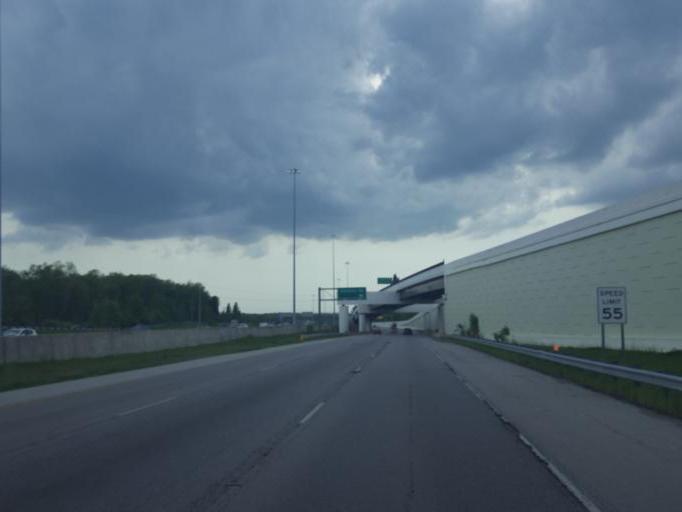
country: US
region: Ohio
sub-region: Franklin County
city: Huber Ridge
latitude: 40.0806
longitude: -82.8790
